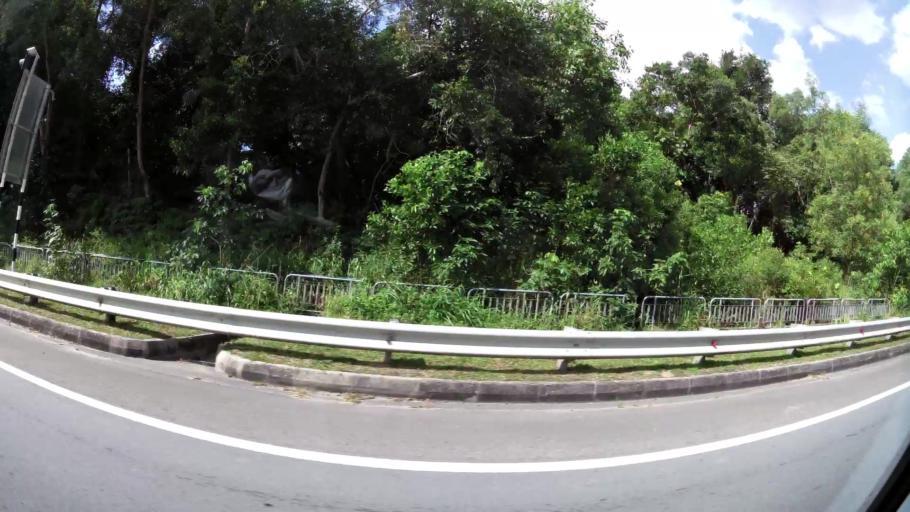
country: BN
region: Brunei and Muara
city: Bandar Seri Begawan
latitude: 4.9521
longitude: 114.9607
